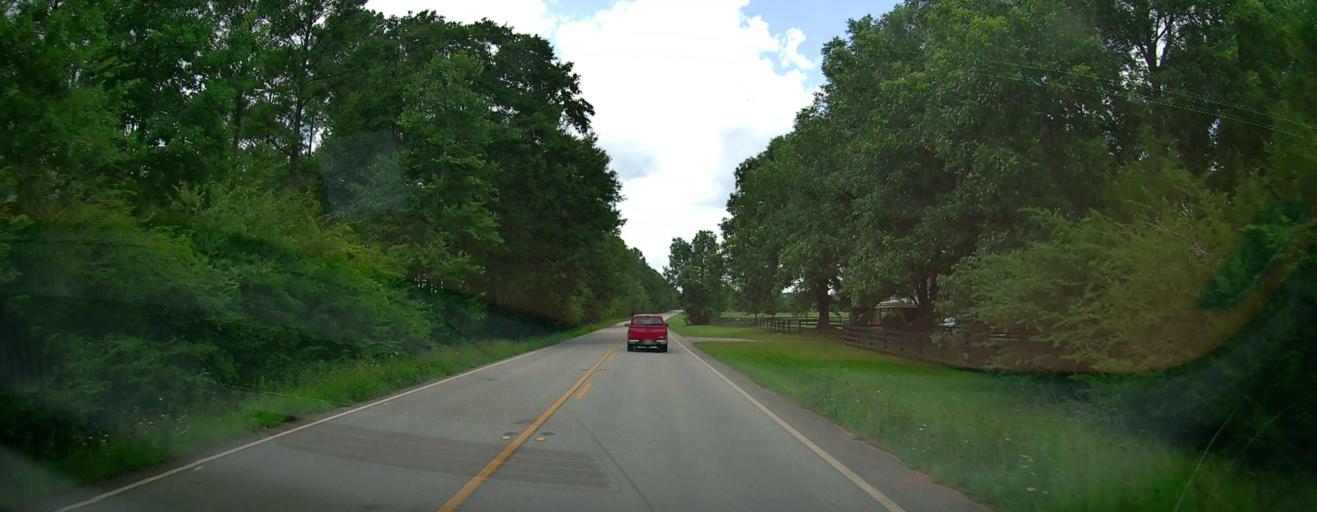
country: US
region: Georgia
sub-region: Meriwether County
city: Greenville
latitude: 33.0624
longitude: -84.7620
